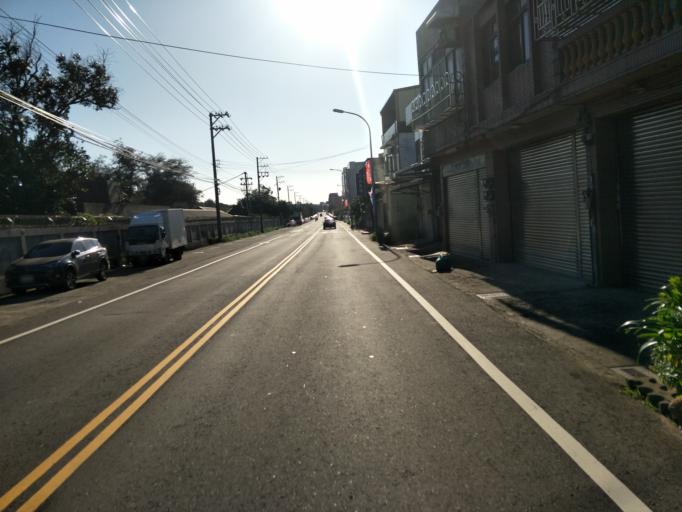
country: TW
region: Taiwan
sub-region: Hsinchu
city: Zhubei
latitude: 24.8742
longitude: 121.0429
